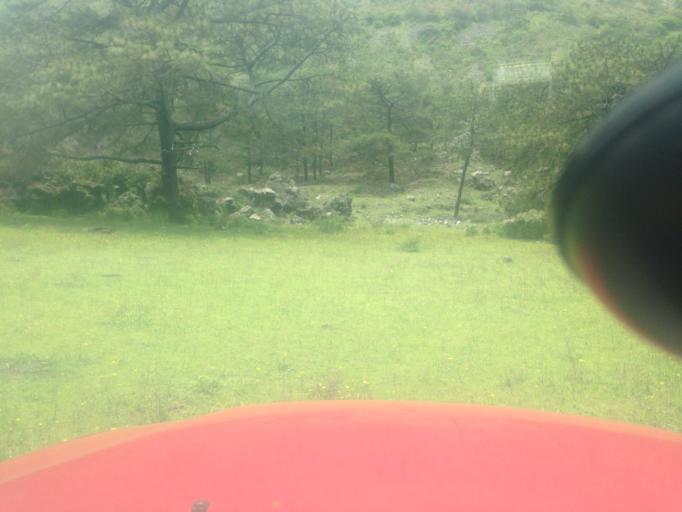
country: MX
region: Nayarit
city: Jala
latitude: 21.1211
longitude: -104.4977
